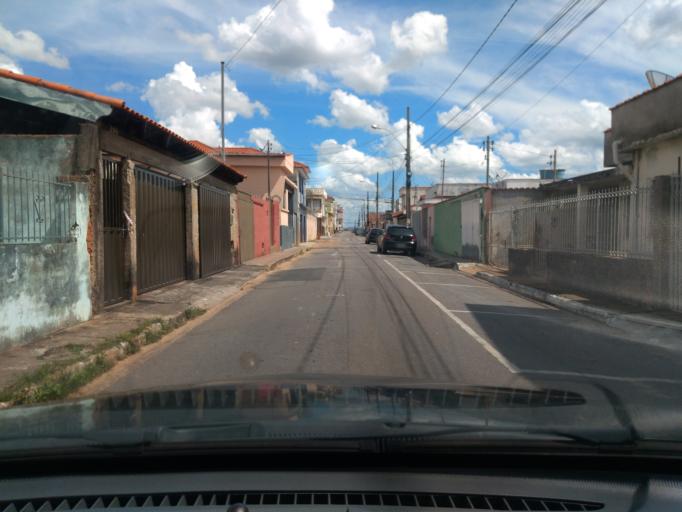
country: BR
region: Minas Gerais
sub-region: Tres Coracoes
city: Tres Coracoes
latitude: -21.6906
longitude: -45.2516
